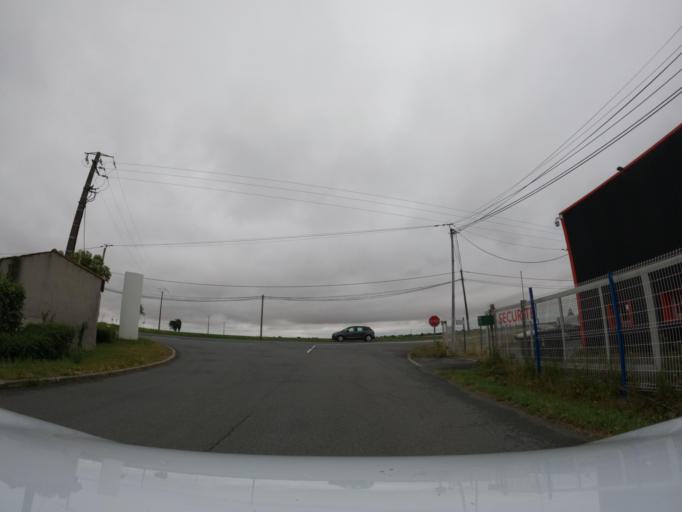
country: FR
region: Pays de la Loire
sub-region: Departement de la Vendee
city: Maillezais
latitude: 46.4233
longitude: -0.7091
